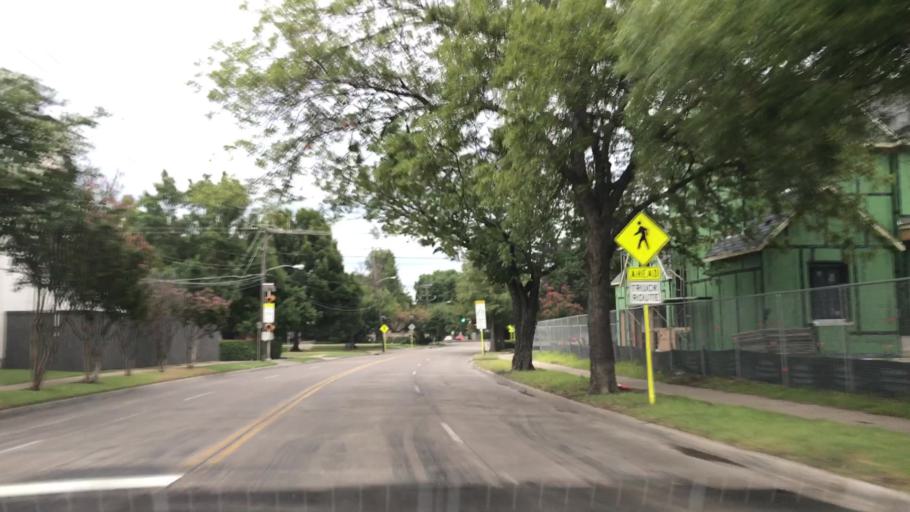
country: US
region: Texas
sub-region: Dallas County
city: University Park
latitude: 32.8591
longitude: -96.7867
